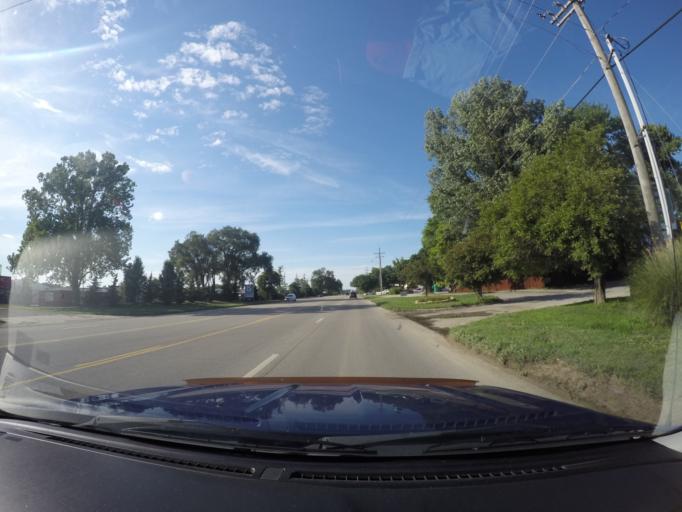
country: US
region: Kansas
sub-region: Douglas County
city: Lawrence
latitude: 38.9942
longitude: -95.2333
